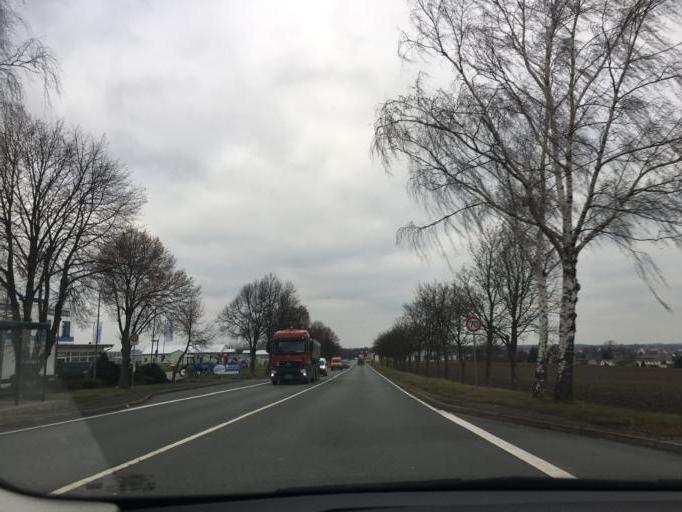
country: DE
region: Saxony
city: Niederfrohna
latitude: 50.9182
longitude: 12.7206
